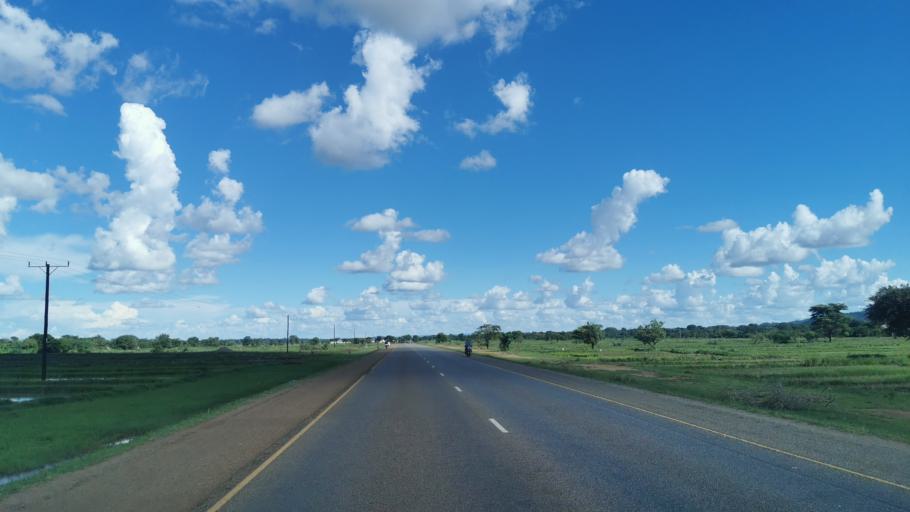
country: TZ
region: Geita
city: Ushirombo
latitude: -3.4789
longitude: 31.9199
